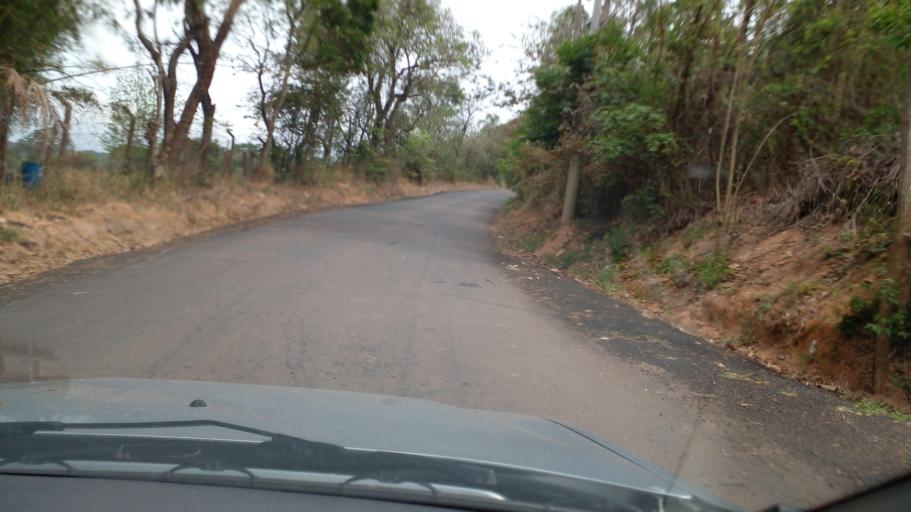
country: BR
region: Sao Paulo
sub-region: Louveira
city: Louveira
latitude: -23.1195
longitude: -46.8949
